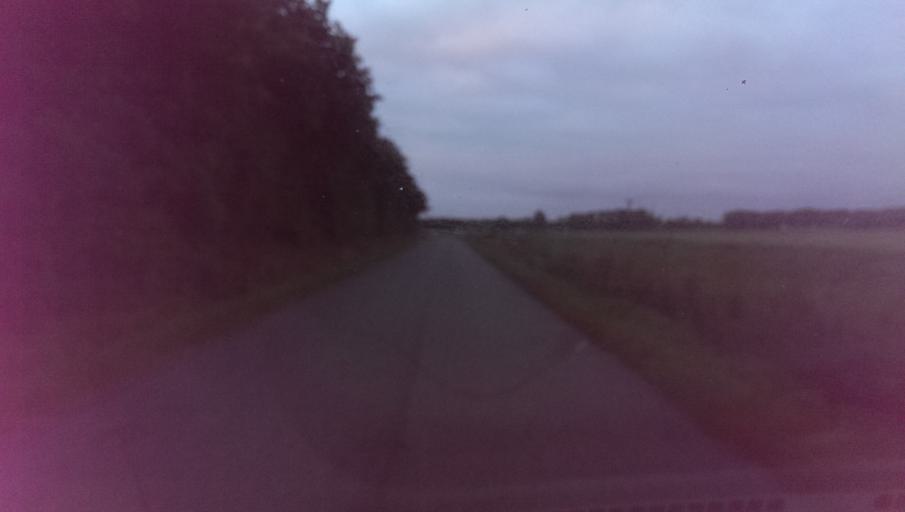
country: DK
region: South Denmark
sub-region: Esbjerg Kommune
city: Tjaereborg
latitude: 55.4843
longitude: 8.5282
